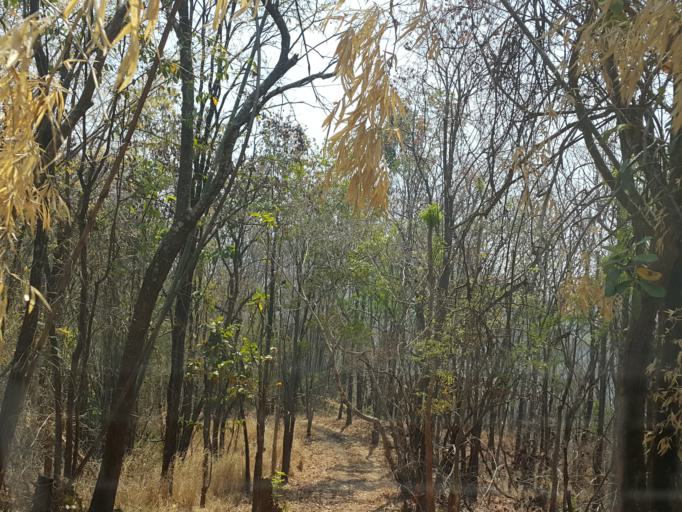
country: TH
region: Chiang Mai
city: Samoeng
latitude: 18.7900
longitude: 98.8236
